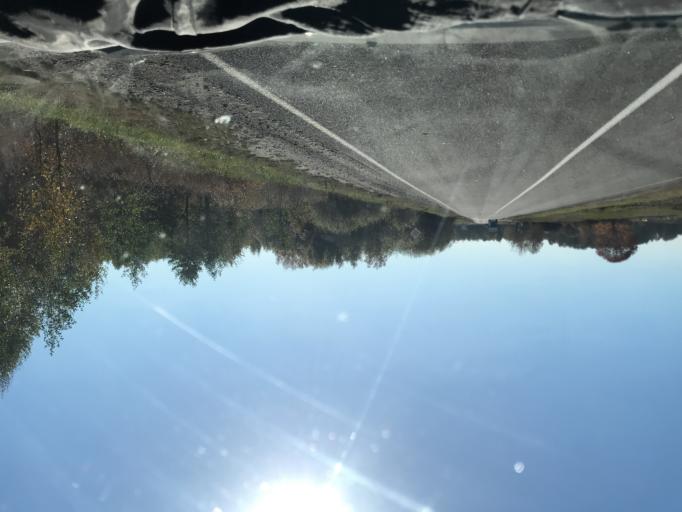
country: BY
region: Gomel
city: Kalinkavichy
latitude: 52.3992
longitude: 29.3047
